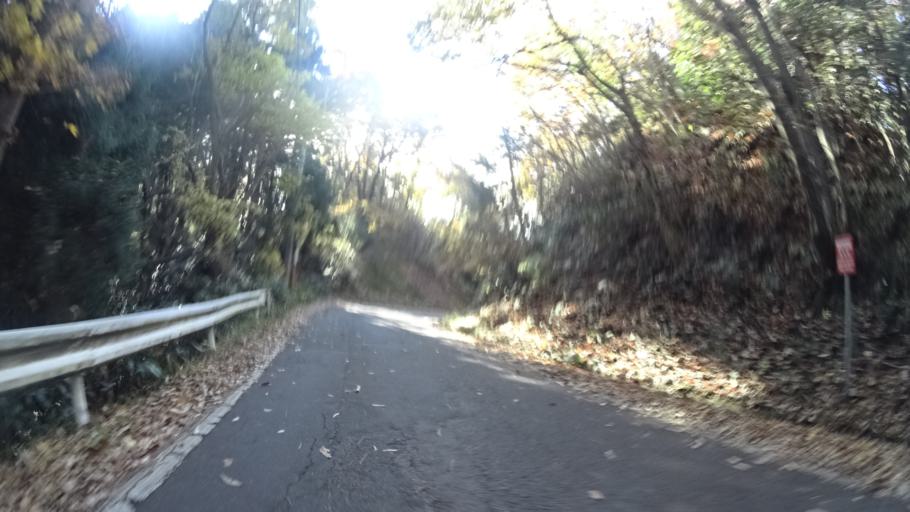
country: JP
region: Niigata
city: Yoshida-kasugacho
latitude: 37.6585
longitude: 138.8136
